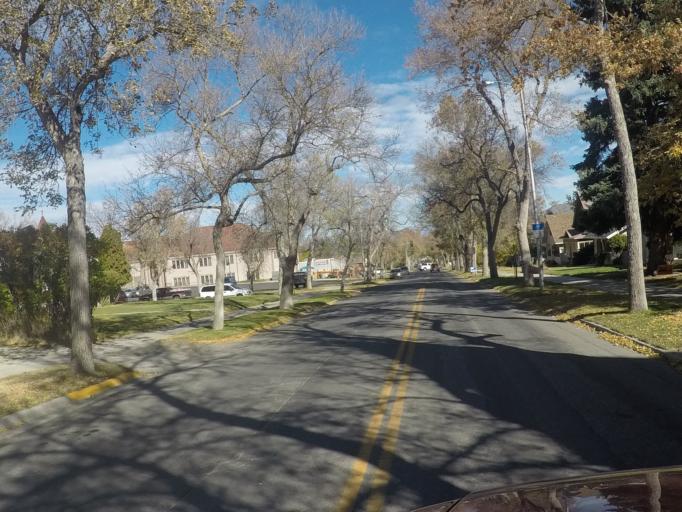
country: US
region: Montana
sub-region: Lewis and Clark County
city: Helena
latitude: 46.5892
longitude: -112.0318
